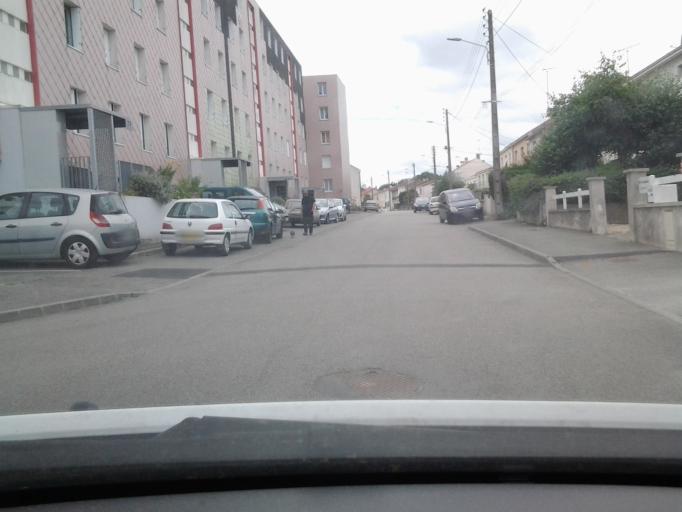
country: FR
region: Pays de la Loire
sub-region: Departement de la Vendee
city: La Roche-sur-Yon
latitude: 46.6641
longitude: -1.4354
